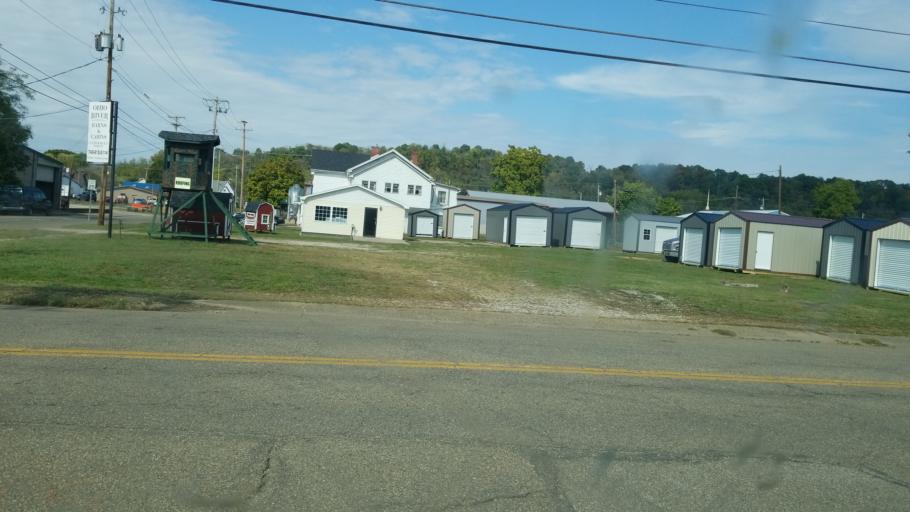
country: US
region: Ohio
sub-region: Gallia County
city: Gallipolis
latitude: 38.8162
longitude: -82.1928
